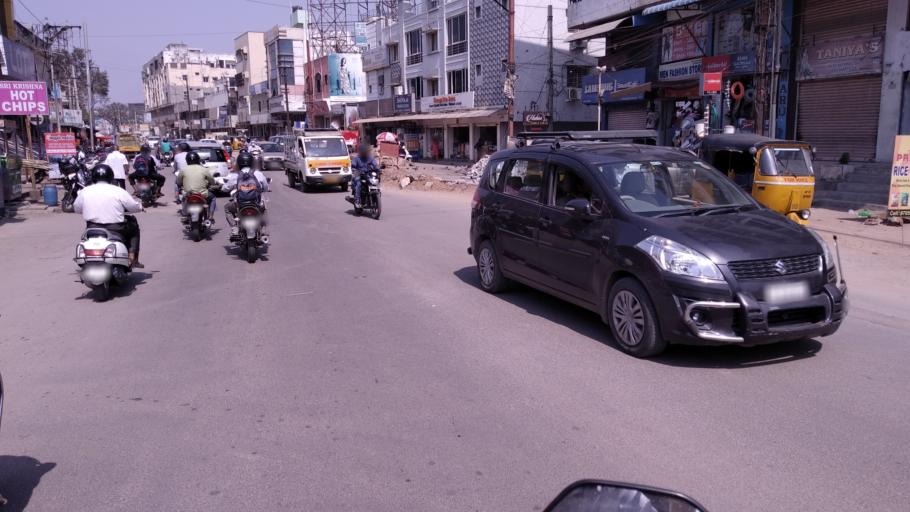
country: IN
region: Telangana
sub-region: Rangareddi
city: Quthbullapur
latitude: 17.4661
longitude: 78.4828
